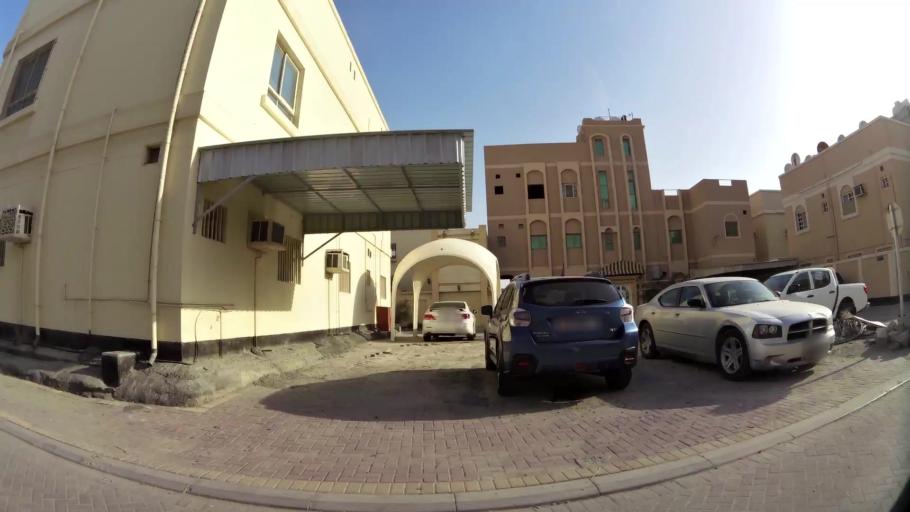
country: BH
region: Manama
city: Jidd Hafs
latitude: 26.2161
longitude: 50.5175
